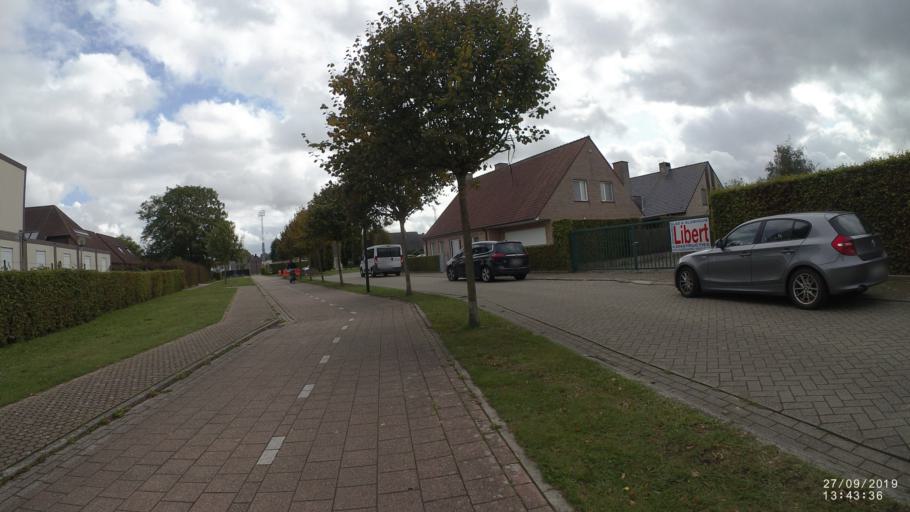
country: BE
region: Flanders
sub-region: Provincie Oost-Vlaanderen
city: Oudenaarde
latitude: 50.8514
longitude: 3.6117
